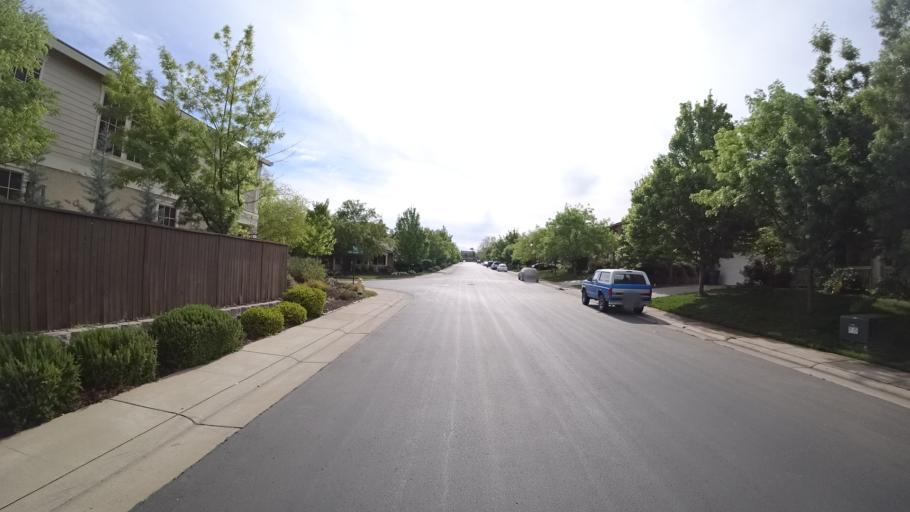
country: US
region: California
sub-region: Placer County
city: Rocklin
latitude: 38.8318
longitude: -121.2774
